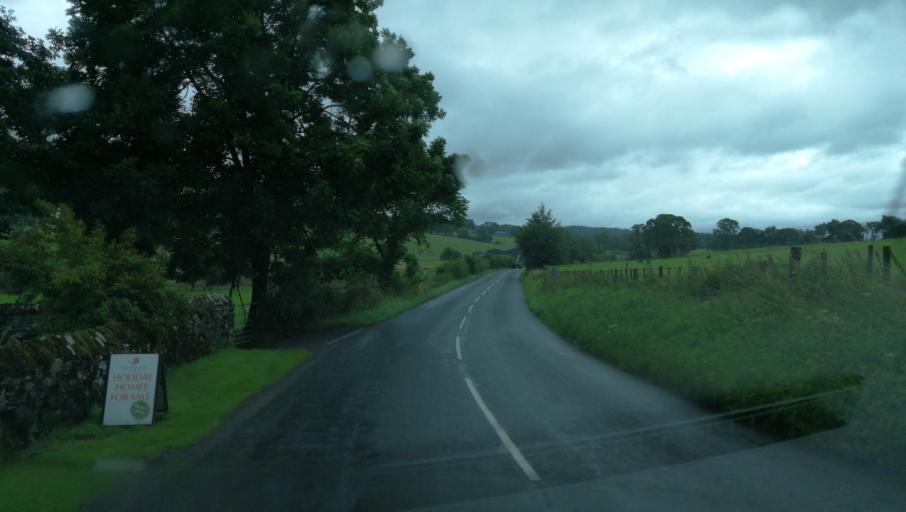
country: GB
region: England
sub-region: Cumbria
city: Penrith
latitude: 54.6138
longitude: -2.8305
